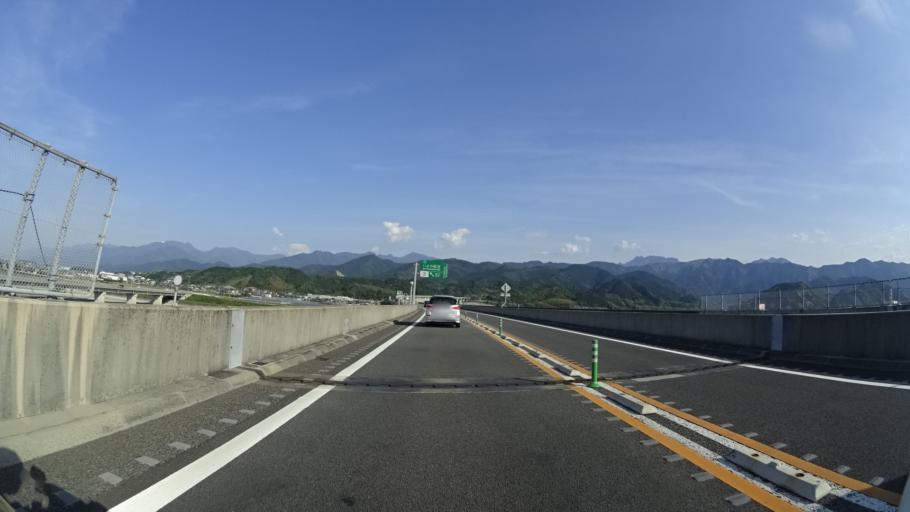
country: JP
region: Ehime
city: Saijo
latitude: 33.8967
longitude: 133.0791
